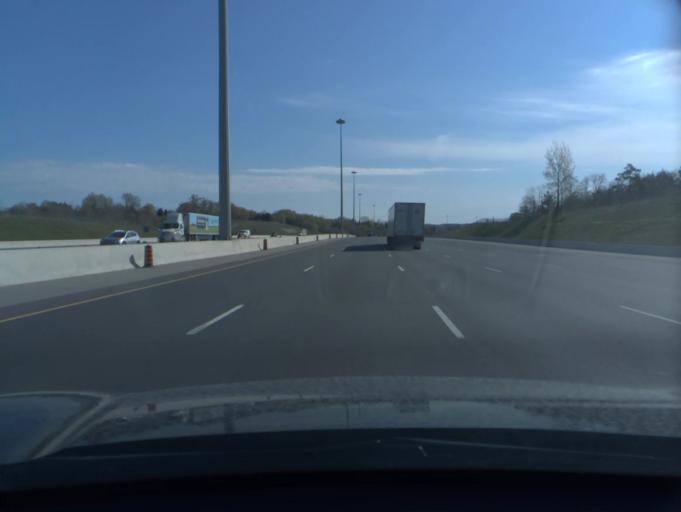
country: CA
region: Ontario
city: North Perth
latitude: 43.8168
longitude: -80.9998
